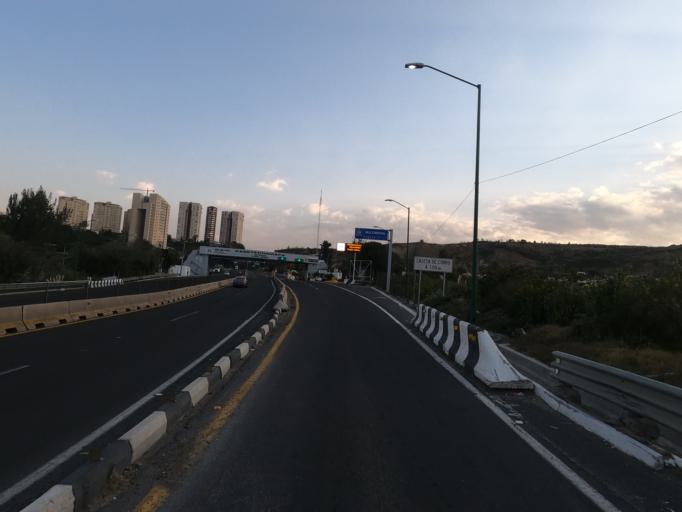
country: MX
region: Mexico
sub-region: Naucalpan de Juarez
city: Ejido el Castillo
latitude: 19.4329
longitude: -99.2972
